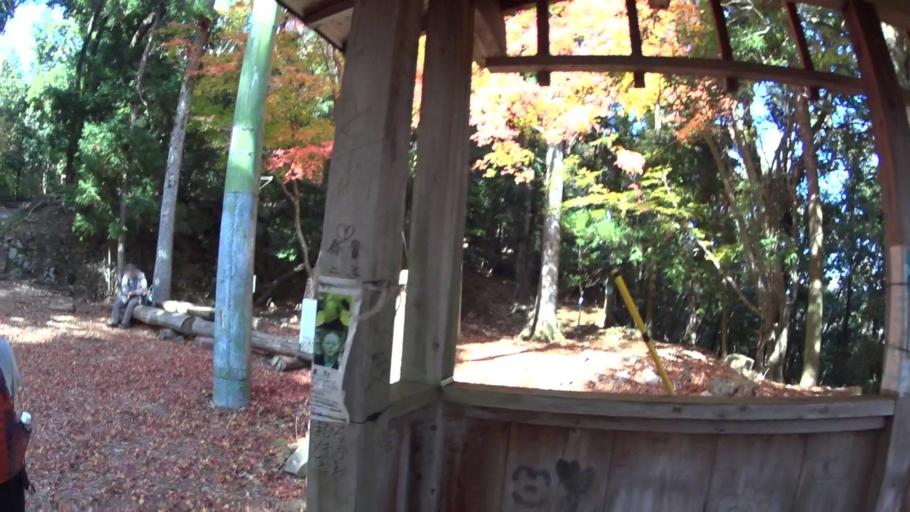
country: JP
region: Kyoto
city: Kameoka
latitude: 35.0438
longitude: 135.6507
